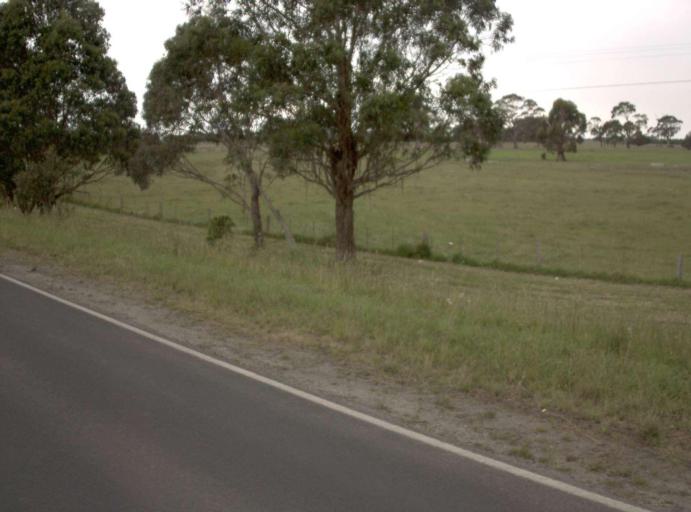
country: AU
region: Victoria
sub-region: Latrobe
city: Traralgon
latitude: -38.5500
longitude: 146.6854
